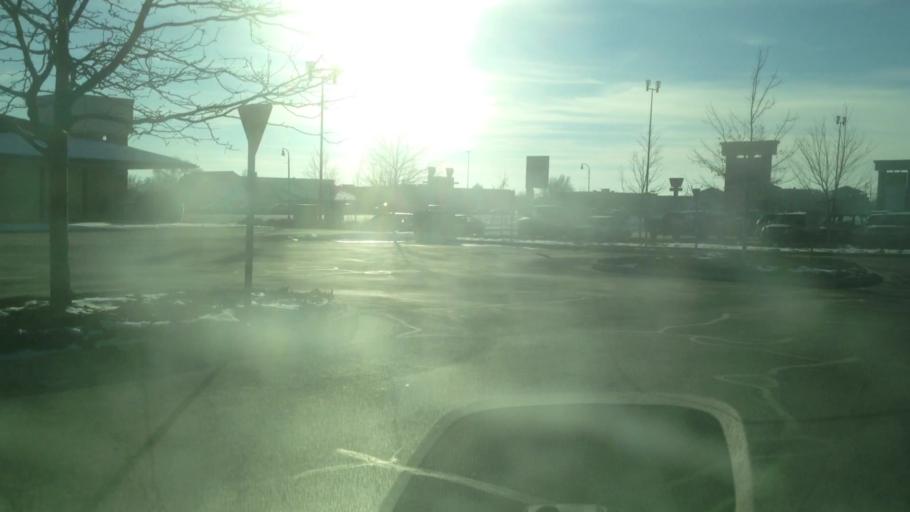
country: US
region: Utah
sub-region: Utah County
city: Orem
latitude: 40.2744
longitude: -111.6870
